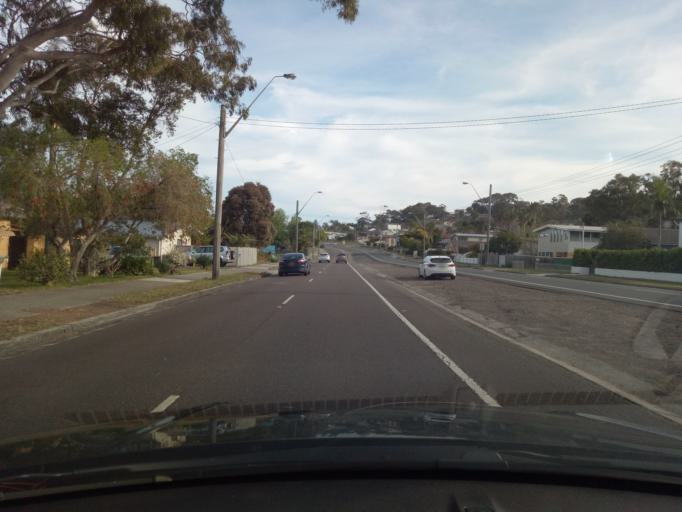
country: AU
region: New South Wales
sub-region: Wyong Shire
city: Bateau Bay
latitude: -33.3828
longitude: 151.4729
